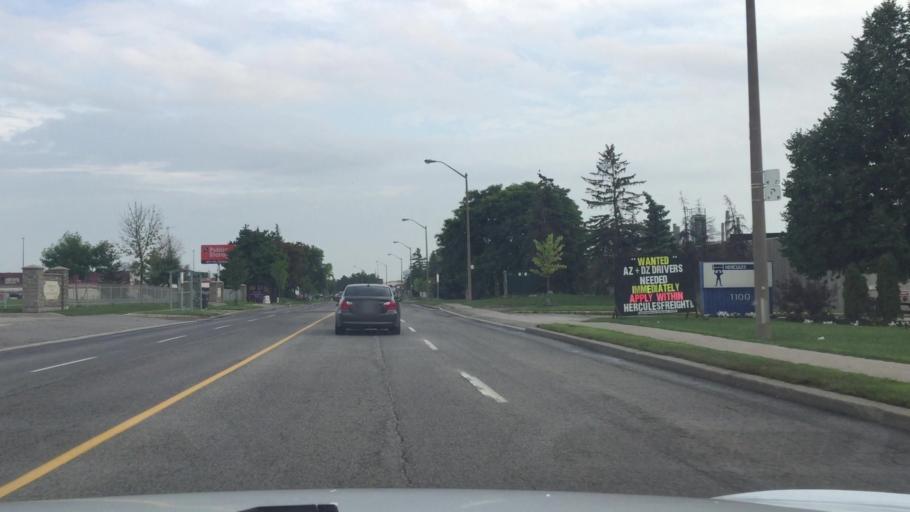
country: CA
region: Ontario
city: Concord
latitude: 43.7516
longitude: -79.5349
